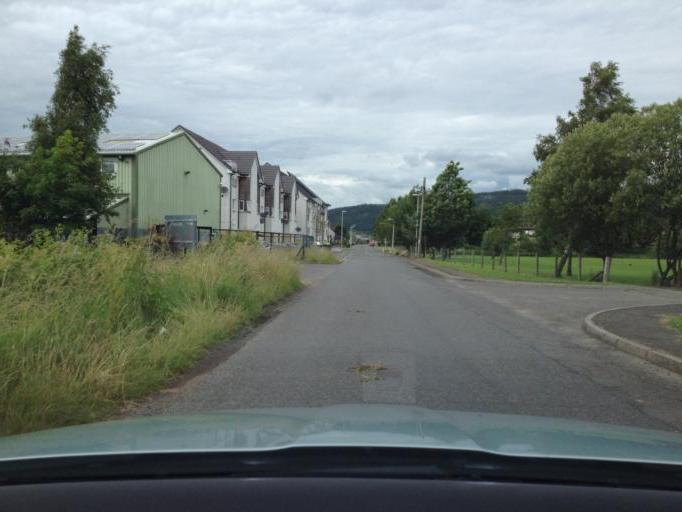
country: GB
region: Scotland
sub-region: Perth and Kinross
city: Bridge of Earn
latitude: 56.3407
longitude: -3.4013
